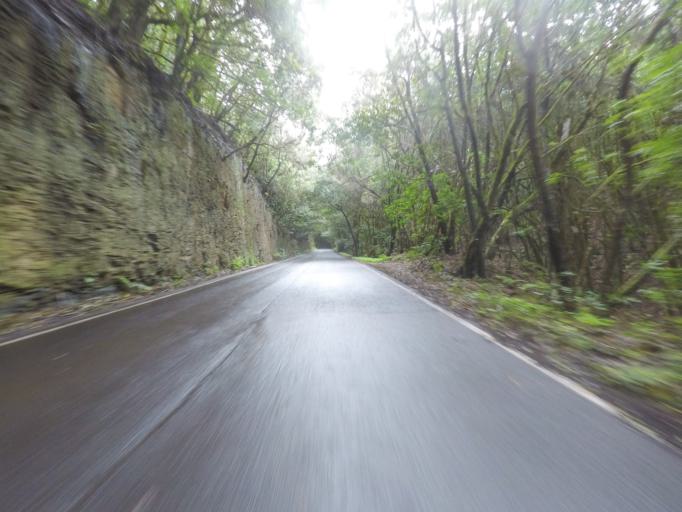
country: ES
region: Canary Islands
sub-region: Provincia de Santa Cruz de Tenerife
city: Vallehermosa
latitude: 28.1601
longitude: -17.2980
